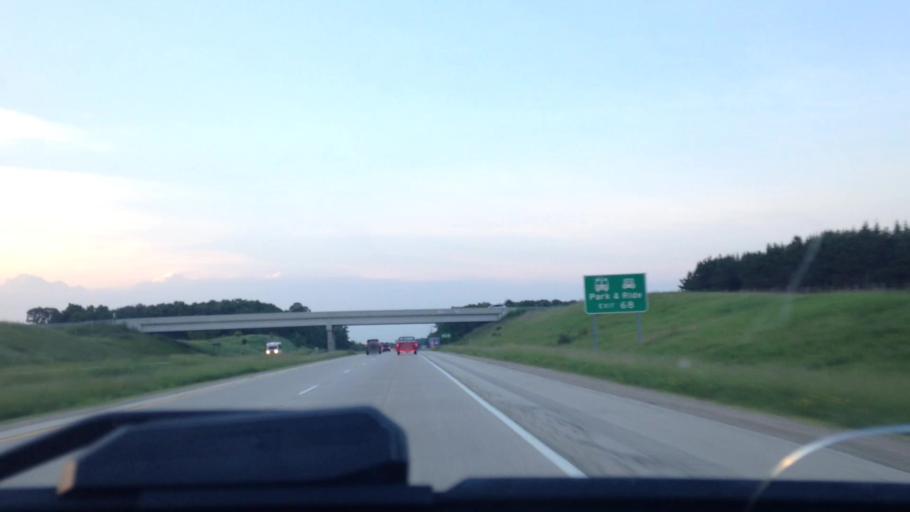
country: US
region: Wisconsin
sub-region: Washington County
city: West Bend
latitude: 43.3817
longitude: -88.1928
